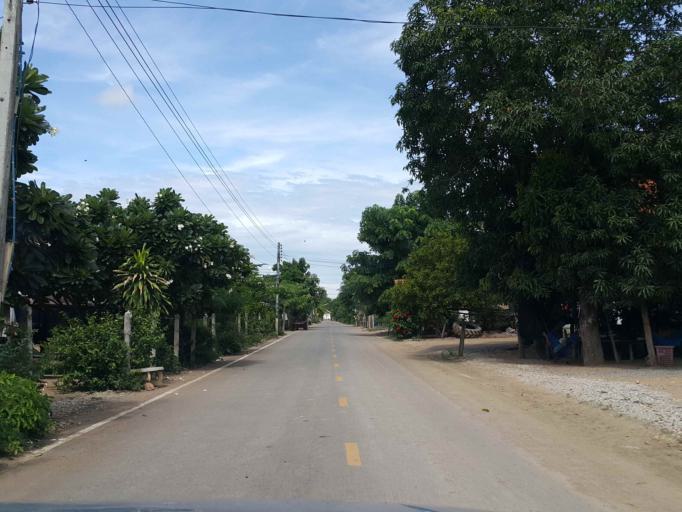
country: TH
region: Sukhothai
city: Ban Dan Lan Hoi
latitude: 17.1084
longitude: 99.4788
